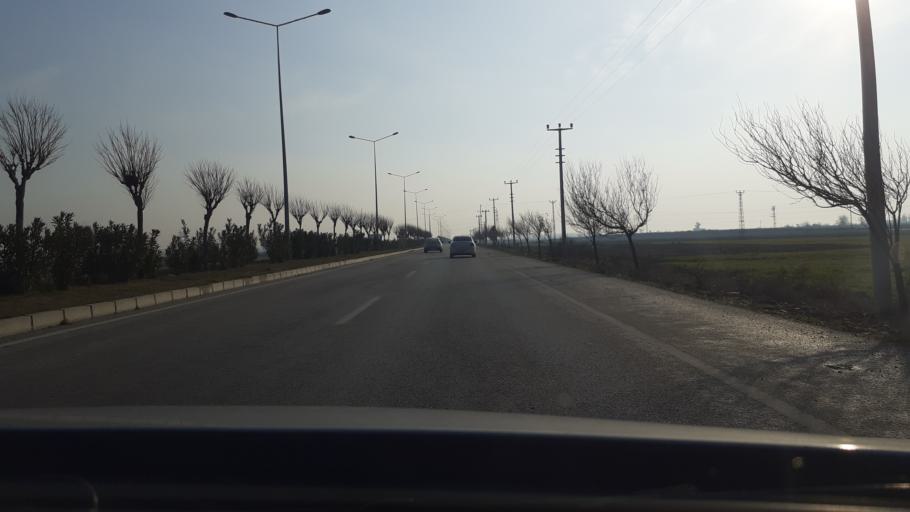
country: TR
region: Hatay
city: Serinyol
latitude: 36.3716
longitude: 36.2378
